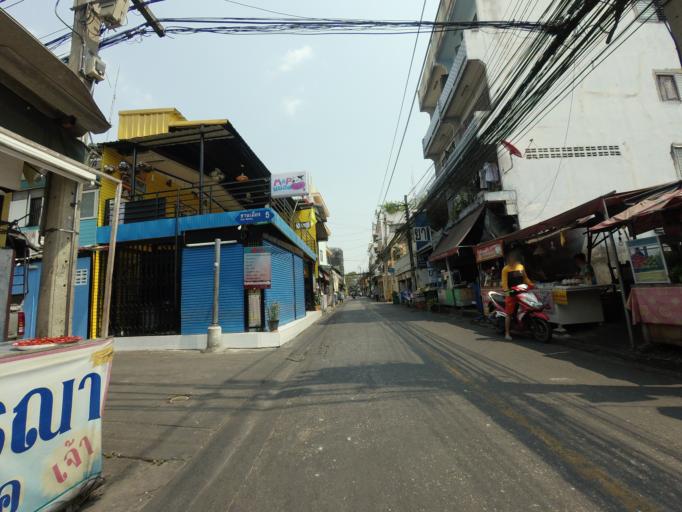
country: TH
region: Bangkok
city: Huai Khwang
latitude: 13.7701
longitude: 100.5679
